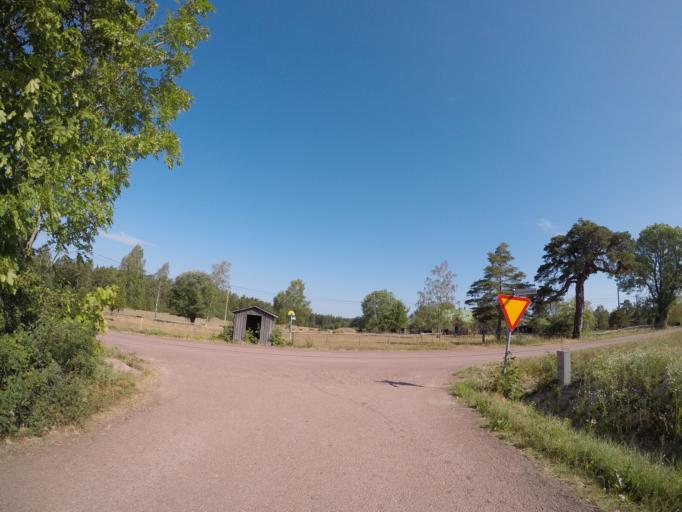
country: AX
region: Alands landsbygd
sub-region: Finstroem
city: Finstroem
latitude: 60.2804
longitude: 19.9567
